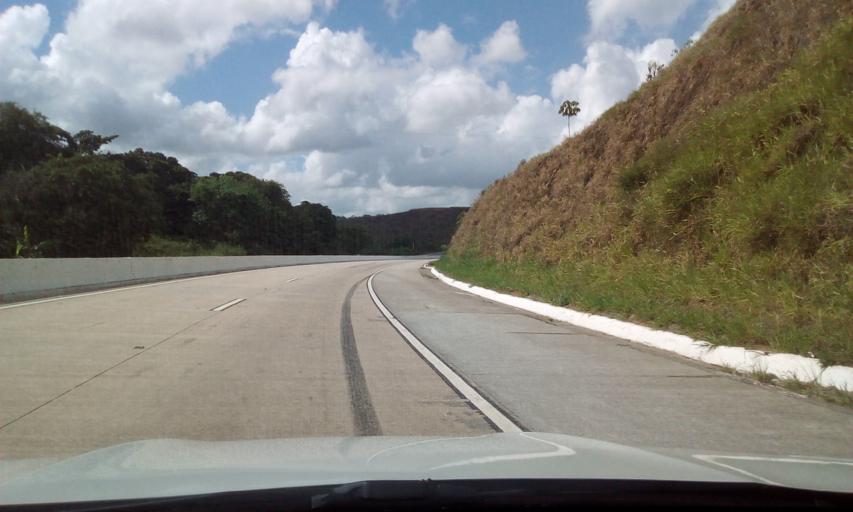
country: BR
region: Pernambuco
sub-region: Palmares
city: Palmares
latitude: -8.7564
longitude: -35.6017
